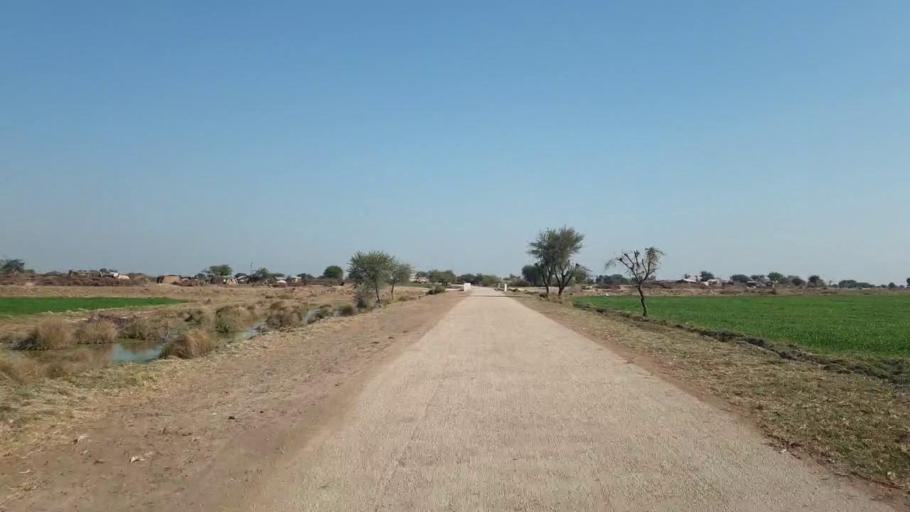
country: PK
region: Sindh
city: Shahdadpur
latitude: 25.9791
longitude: 68.6615
